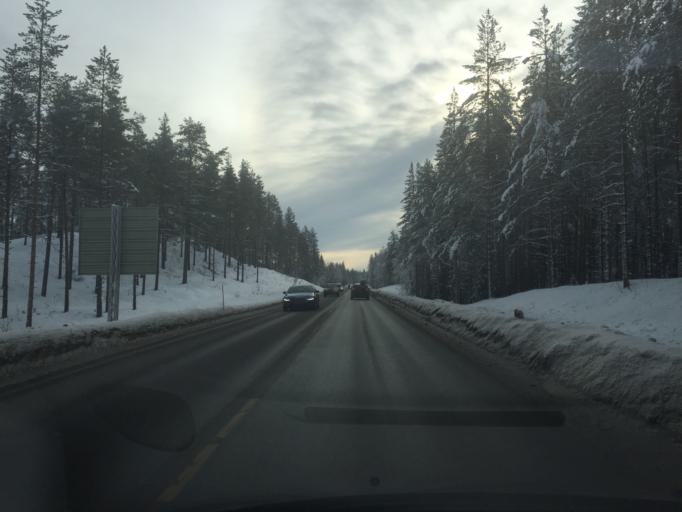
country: NO
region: Hedmark
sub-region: Trysil
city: Innbygda
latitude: 61.2920
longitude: 12.2734
